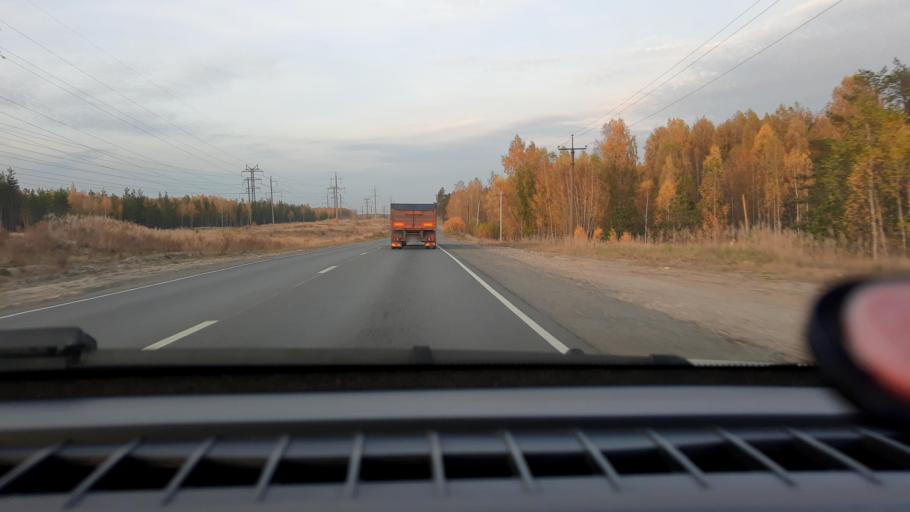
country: RU
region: Nizjnij Novgorod
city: Lukino
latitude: 56.3417
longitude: 43.5810
